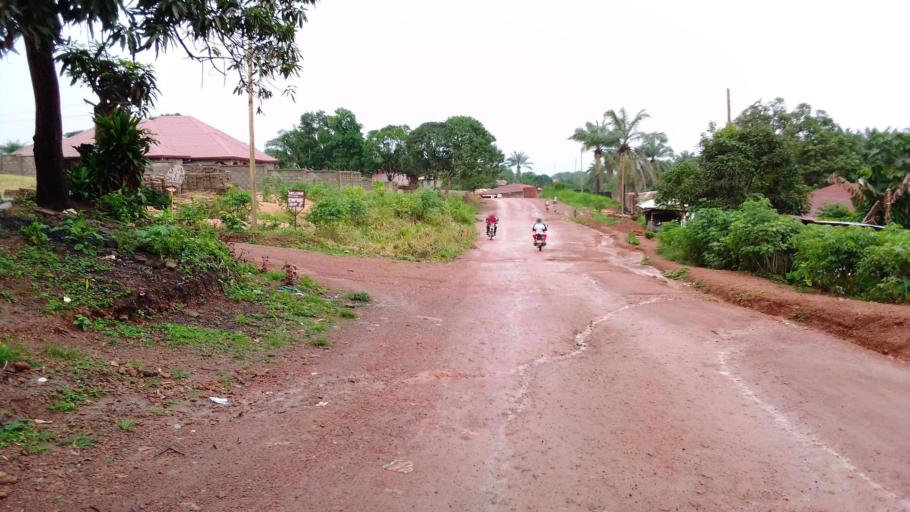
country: SL
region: Eastern Province
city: Kenema
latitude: 7.8765
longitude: -11.1637
